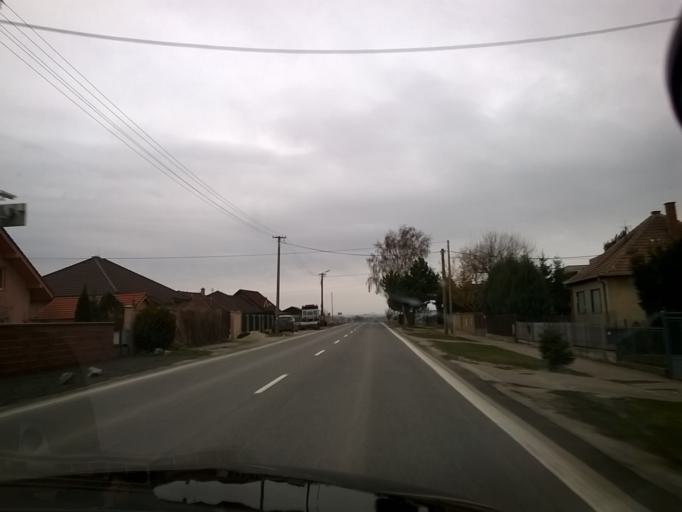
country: SK
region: Nitriansky
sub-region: Okres Nitra
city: Nitra
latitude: 48.3799
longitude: 18.0535
